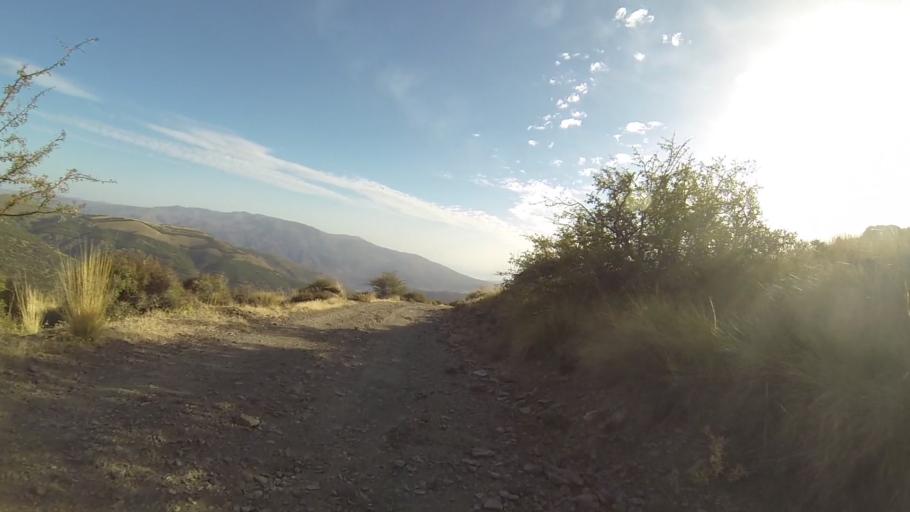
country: ES
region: Andalusia
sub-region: Provincia de Almeria
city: Laujar de Andarax
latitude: 37.0662
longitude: -2.8867
